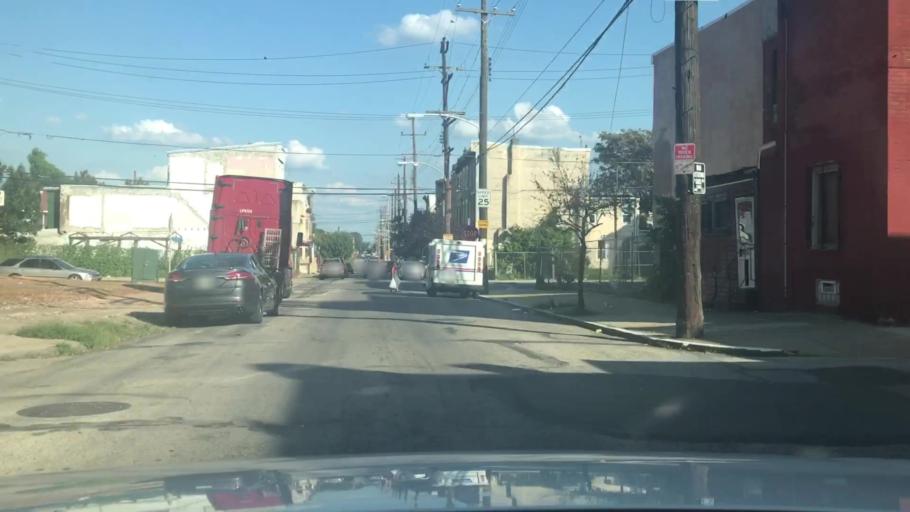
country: US
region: Pennsylvania
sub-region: Philadelphia County
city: Philadelphia
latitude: 39.9890
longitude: -75.1405
